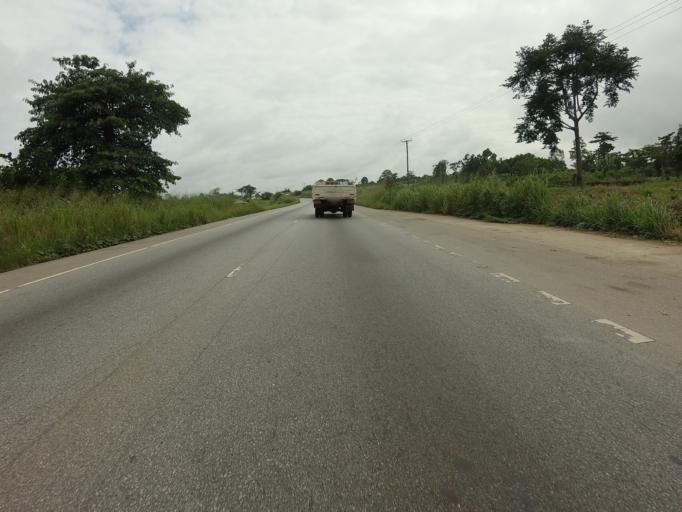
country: GH
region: Ashanti
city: Tafo
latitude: 6.9828
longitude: -1.6878
